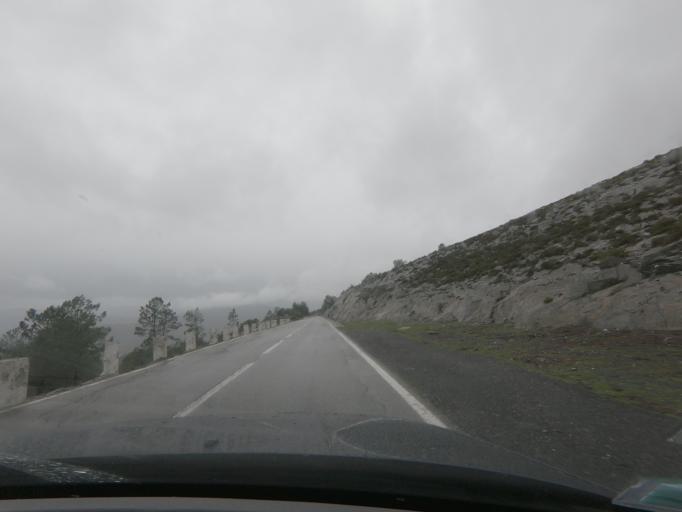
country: PT
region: Vila Real
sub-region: Mondim de Basto
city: Mondim de Basto
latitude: 41.3342
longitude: -7.8766
